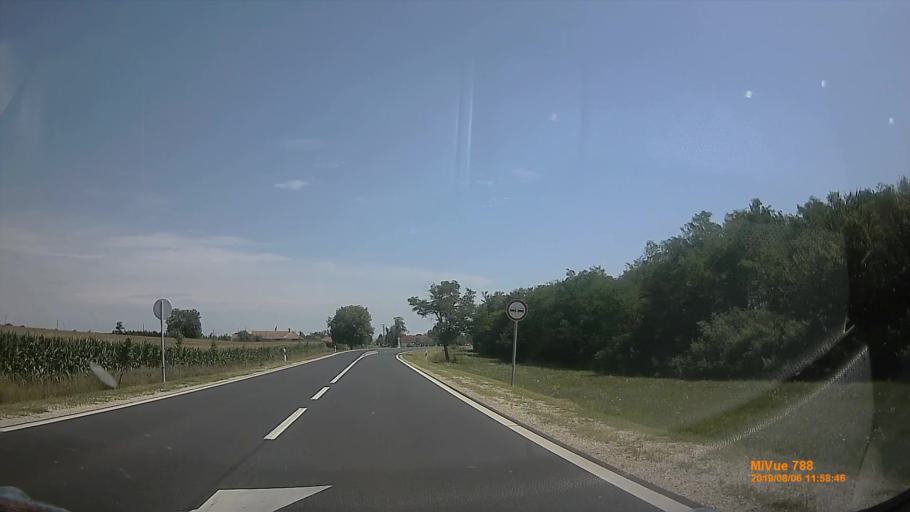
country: HU
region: Vas
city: Vasvar
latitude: 47.0687
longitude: 16.7317
